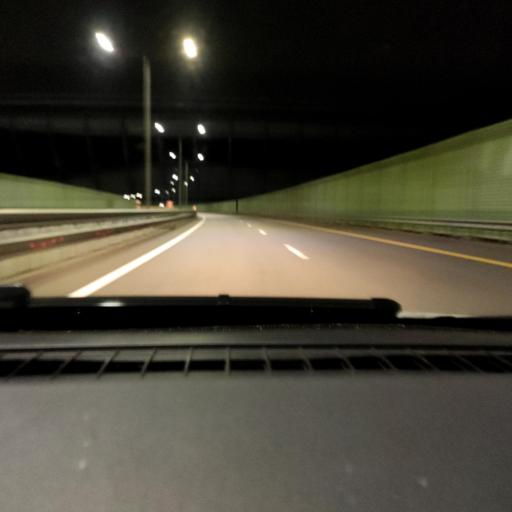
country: RU
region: Voronezj
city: Novaya Usman'
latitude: 51.6108
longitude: 39.3202
